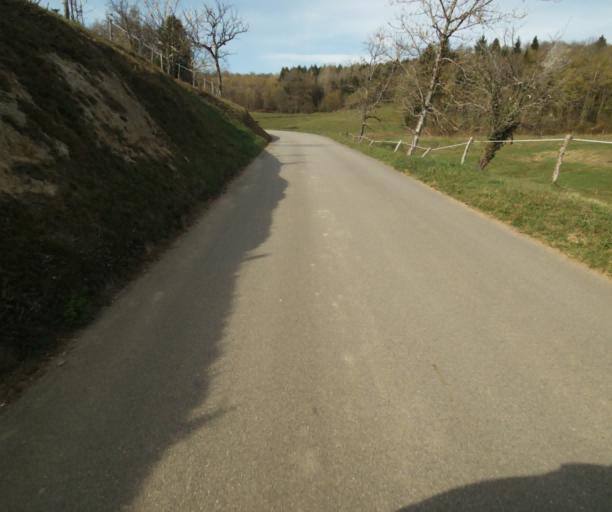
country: FR
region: Limousin
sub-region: Departement de la Correze
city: Naves
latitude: 45.3224
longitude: 1.7252
